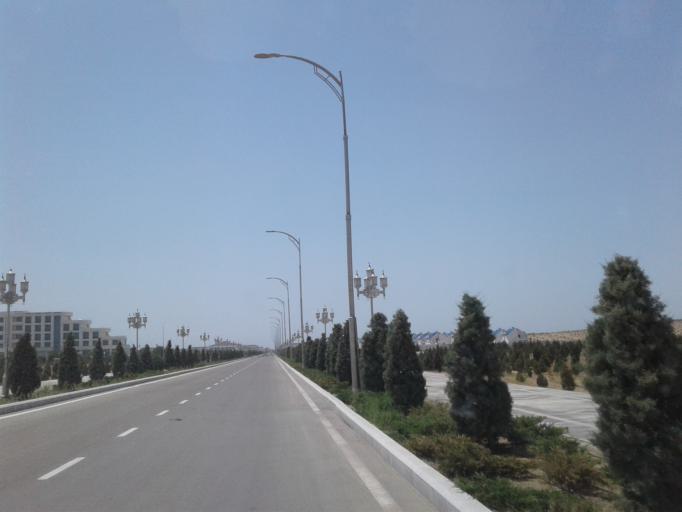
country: TM
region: Balkan
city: Turkmenbasy
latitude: 39.9877
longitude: 52.8330
